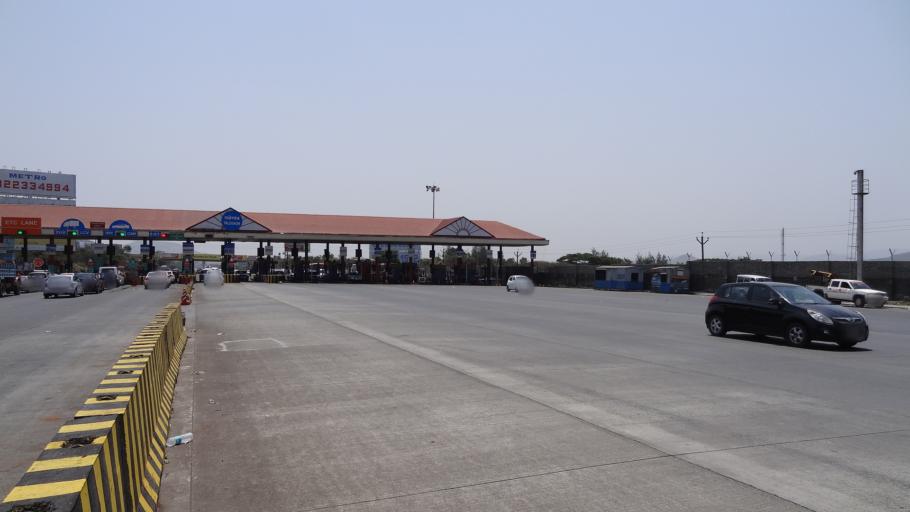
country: IN
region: Maharashtra
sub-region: Pune Division
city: Wadgaon
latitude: 18.7144
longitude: 73.6452
